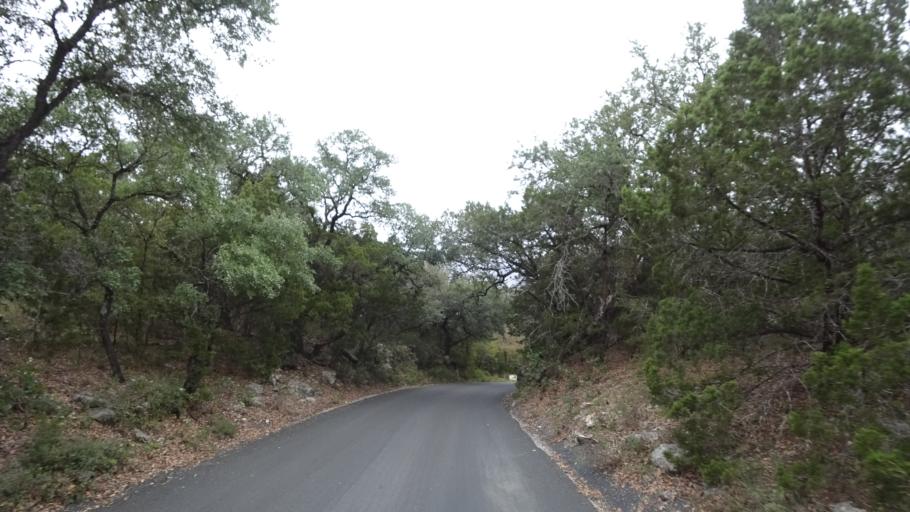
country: US
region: Texas
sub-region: Travis County
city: Bee Cave
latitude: 30.3437
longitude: -97.9311
